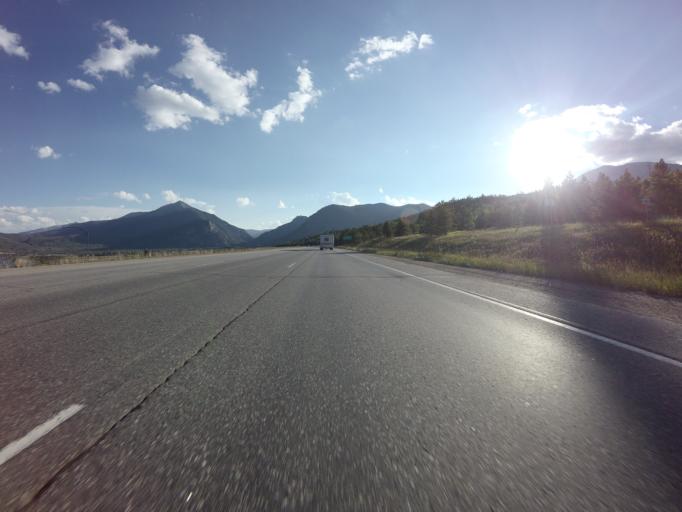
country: US
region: Colorado
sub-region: Summit County
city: Frisco
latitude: 39.6026
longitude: -106.0867
